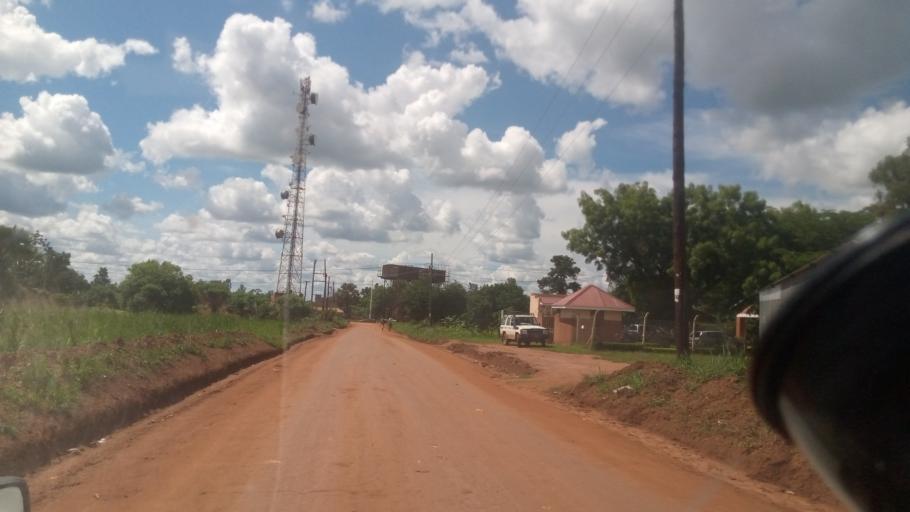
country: UG
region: Northern Region
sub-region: Lira District
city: Lira
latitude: 2.2340
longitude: 32.9040
